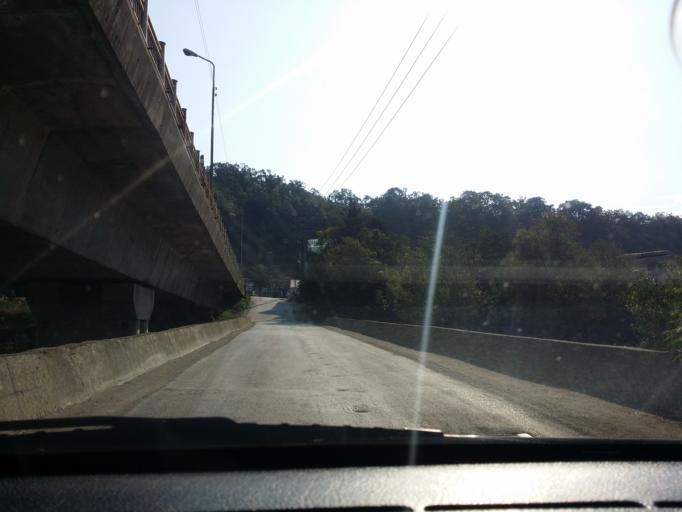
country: IR
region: Mazandaran
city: Chalus
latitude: 36.6471
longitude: 51.4119
